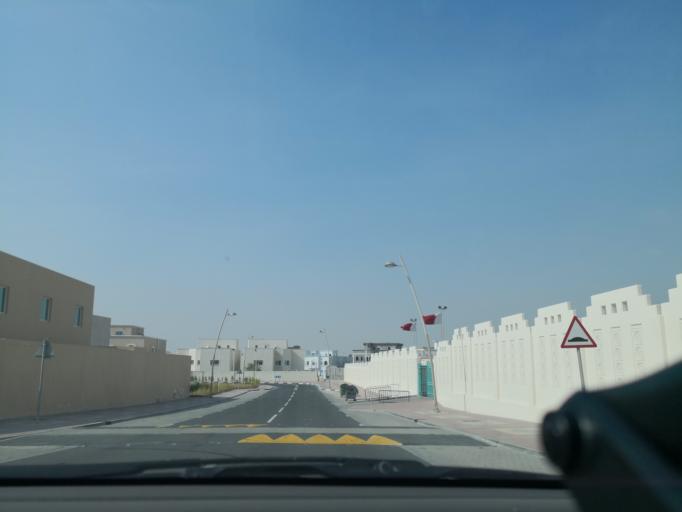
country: QA
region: Baladiyat ad Dawhah
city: Doha
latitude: 25.3445
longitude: 51.4956
